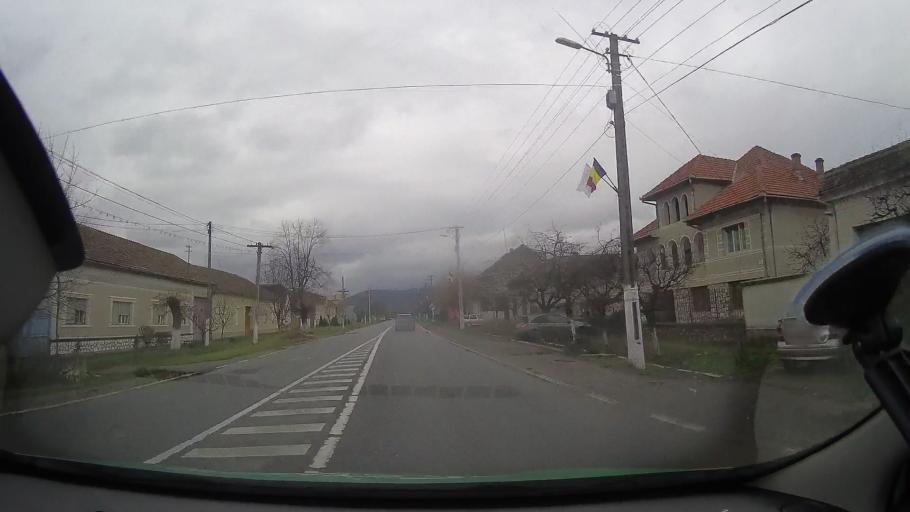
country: RO
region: Arad
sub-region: Comuna Buteni
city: Buteni
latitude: 46.3252
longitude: 22.1240
